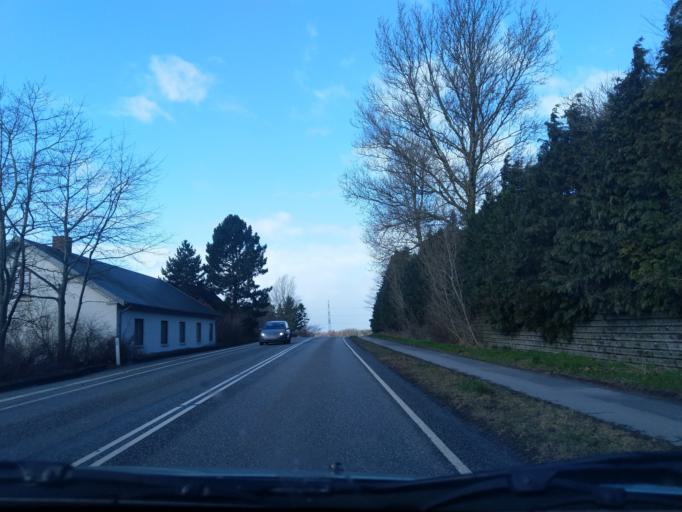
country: DK
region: Zealand
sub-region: Naestved Kommune
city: Naestved
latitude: 55.2769
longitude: 11.7246
